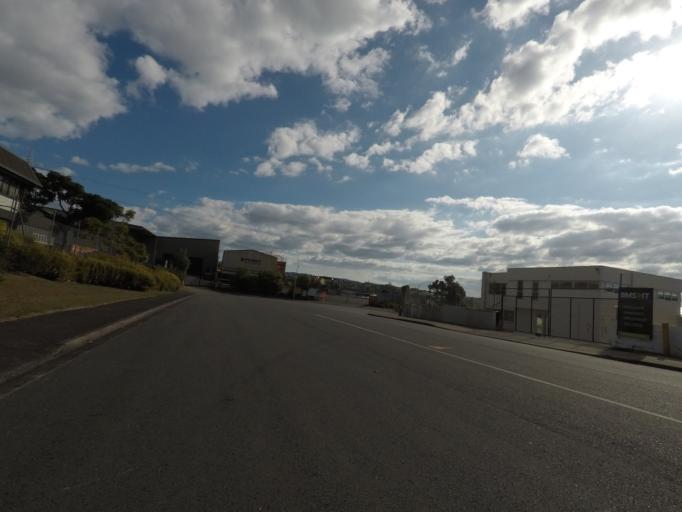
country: NZ
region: Auckland
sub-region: Auckland
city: Rosebank
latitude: -36.8774
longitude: 174.6669
